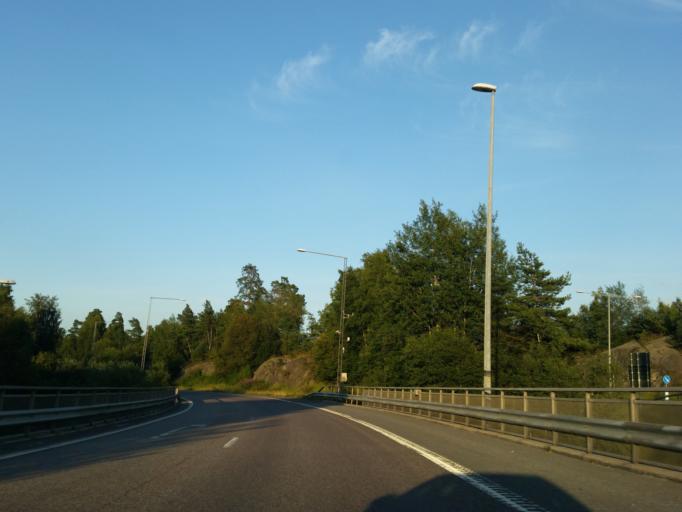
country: SE
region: Stockholm
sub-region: Sodertalje Kommun
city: Soedertaelje
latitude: 59.1992
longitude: 17.6622
